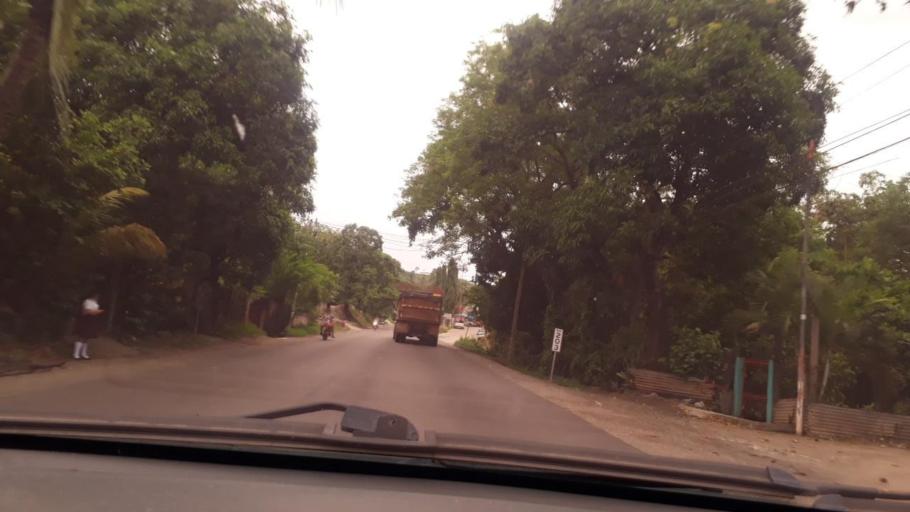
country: GT
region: Izabal
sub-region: Municipio de Los Amates
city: Los Amates
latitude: 15.2714
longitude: -89.0808
